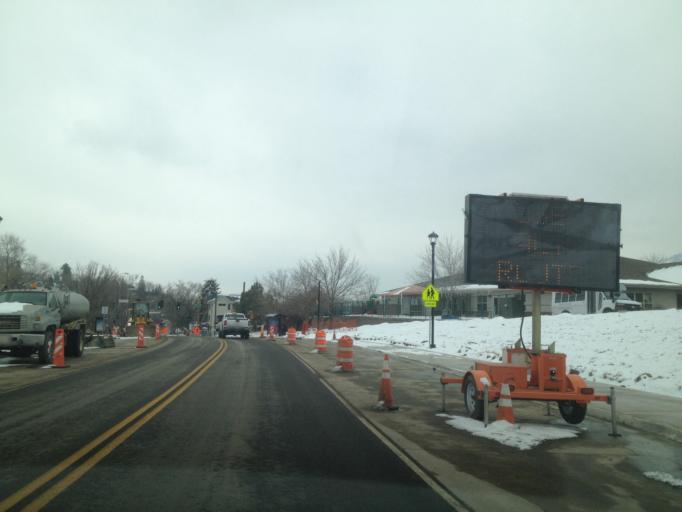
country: US
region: Colorado
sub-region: Jefferson County
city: Golden
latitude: 39.7663
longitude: -105.2322
